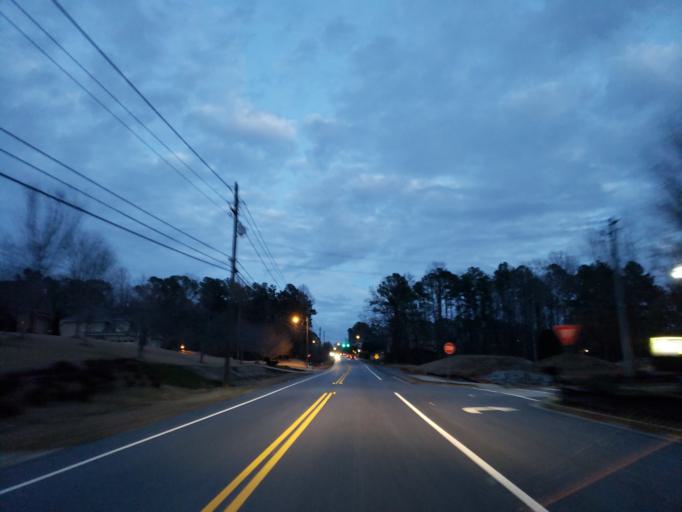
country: US
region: Georgia
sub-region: Cobb County
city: Kennesaw
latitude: 33.9987
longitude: -84.6602
